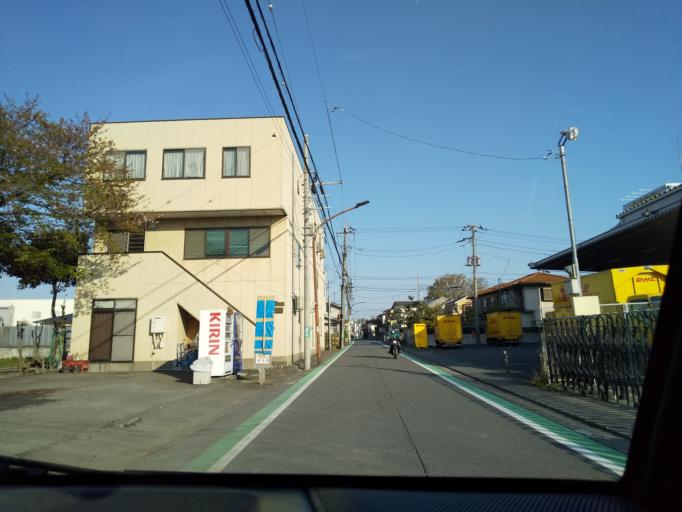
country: JP
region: Tokyo
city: Hino
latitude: 35.6691
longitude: 139.4394
